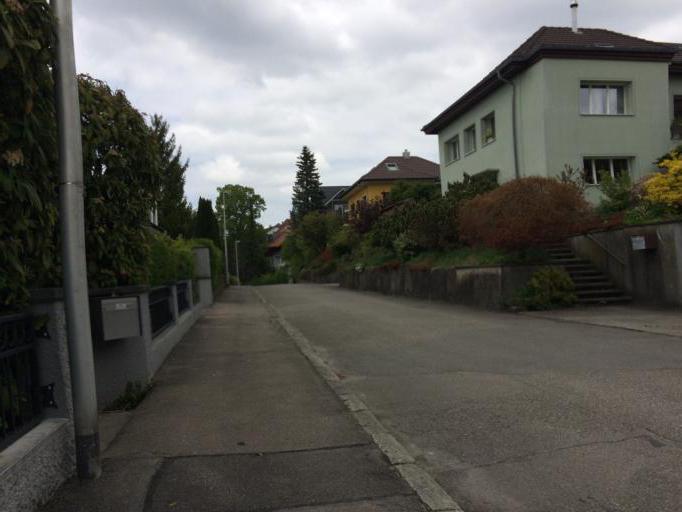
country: CH
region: Bern
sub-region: Bern-Mittelland District
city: Koniz
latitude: 46.9254
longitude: 7.4223
